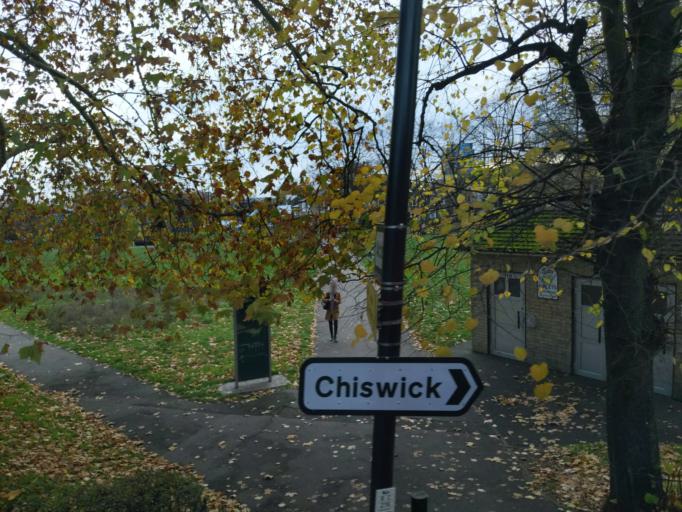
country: GB
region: England
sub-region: Greater London
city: Acton
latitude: 51.4962
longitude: -0.2640
